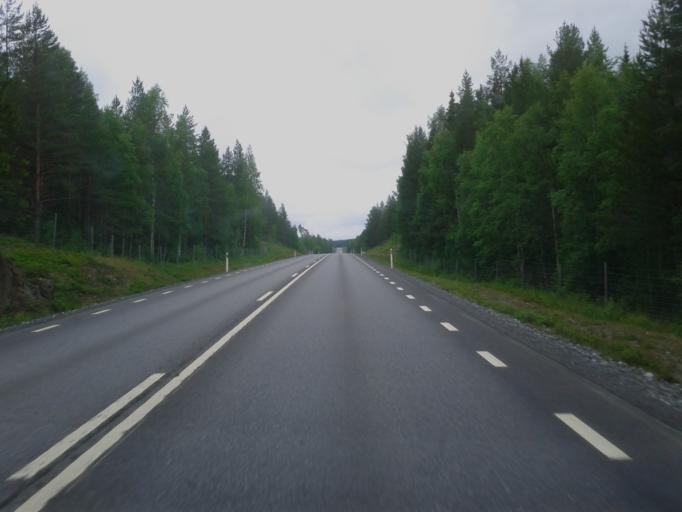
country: SE
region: Vaesterbotten
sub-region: Skelleftea Kommun
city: Boliden
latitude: 64.8733
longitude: 20.4267
